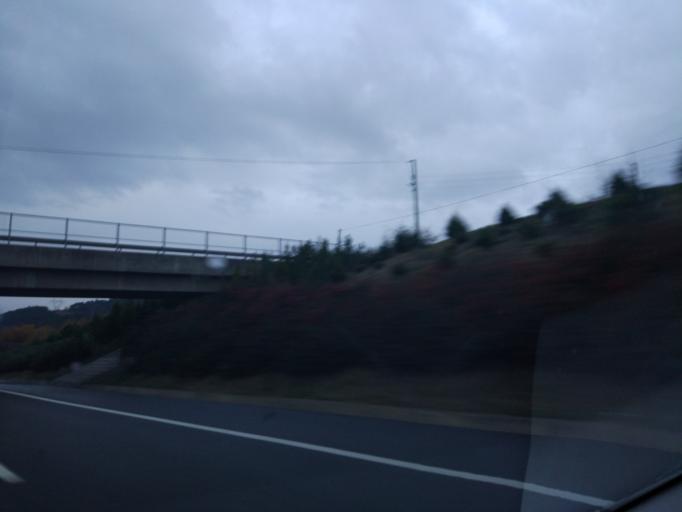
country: TR
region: Duzce
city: Kaynasli
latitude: 40.7805
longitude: 31.3431
